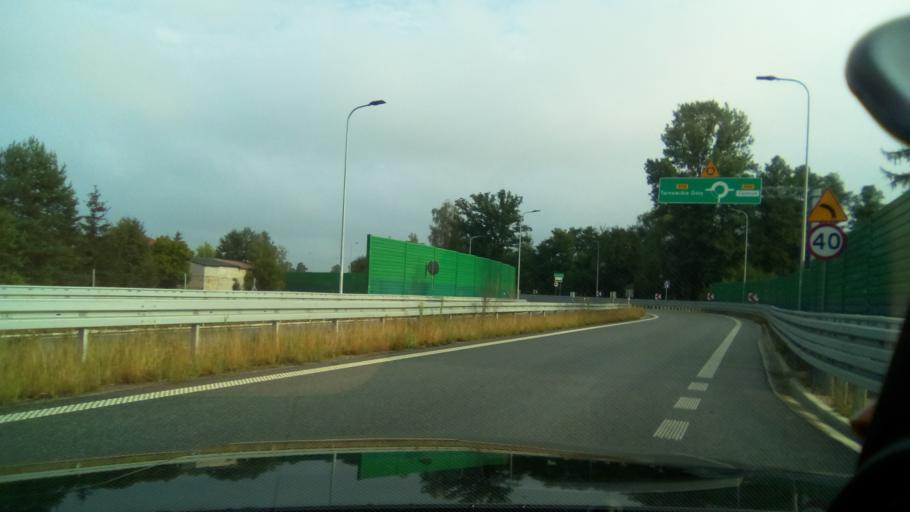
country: PL
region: Silesian Voivodeship
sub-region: Powiat czestochowski
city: Konopiska
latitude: 50.7480
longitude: 19.0484
